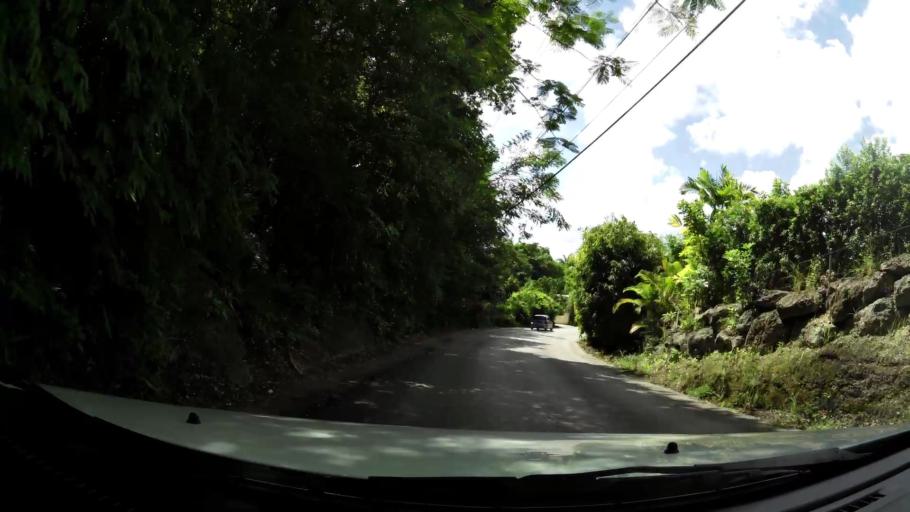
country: BB
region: Saint James
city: Holetown
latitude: 13.2000
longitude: -59.6350
